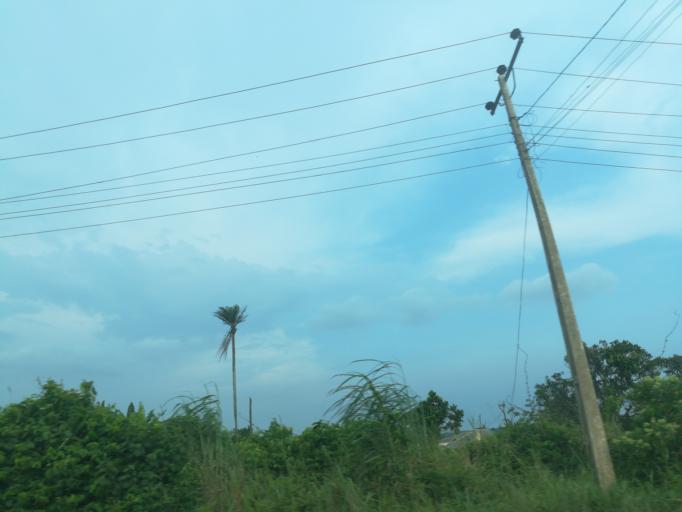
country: NG
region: Lagos
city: Ikorodu
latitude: 6.6405
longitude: 3.6704
